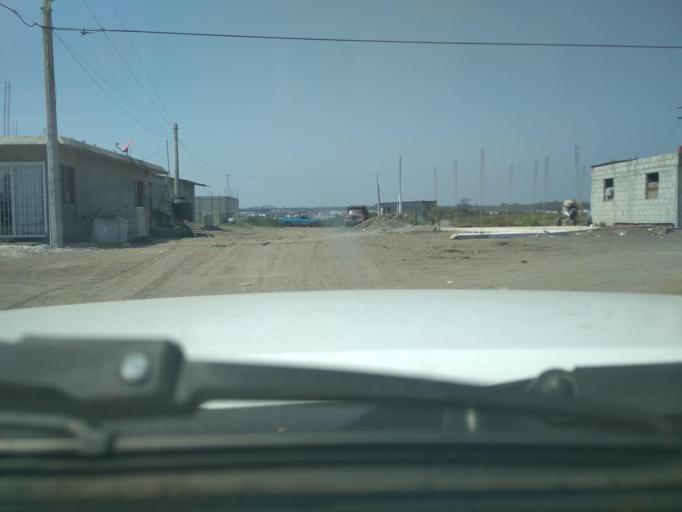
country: MX
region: Veracruz
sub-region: Veracruz
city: Lomas de Rio Medio Cuatro
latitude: 19.1913
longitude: -96.1989
